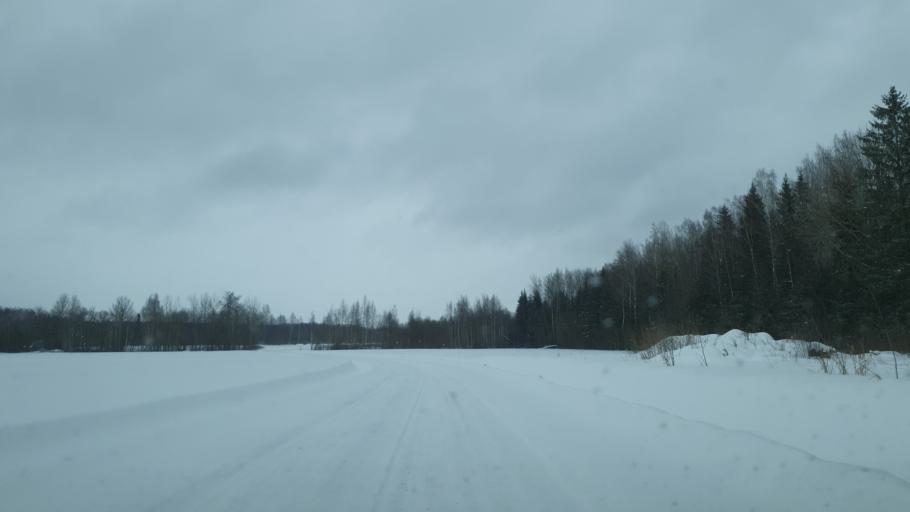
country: EE
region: Polvamaa
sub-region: Raepina vald
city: Rapina
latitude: 58.2063
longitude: 27.3006
